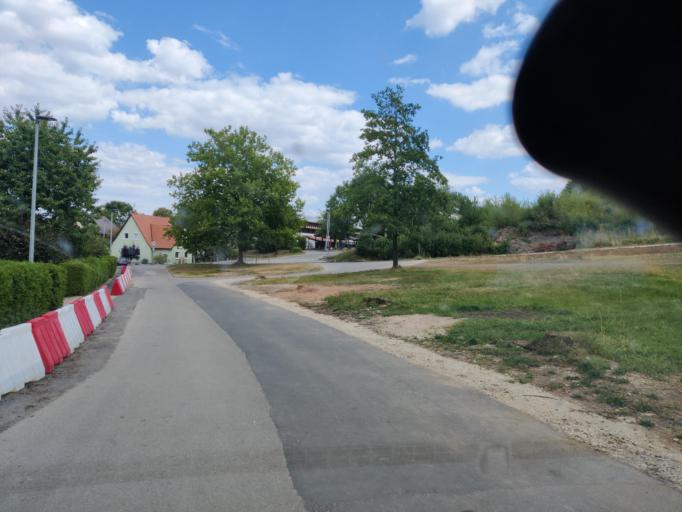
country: DE
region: Bavaria
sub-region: Regierungsbezirk Mittelfranken
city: Thalmassing
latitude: 49.0810
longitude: 11.2137
